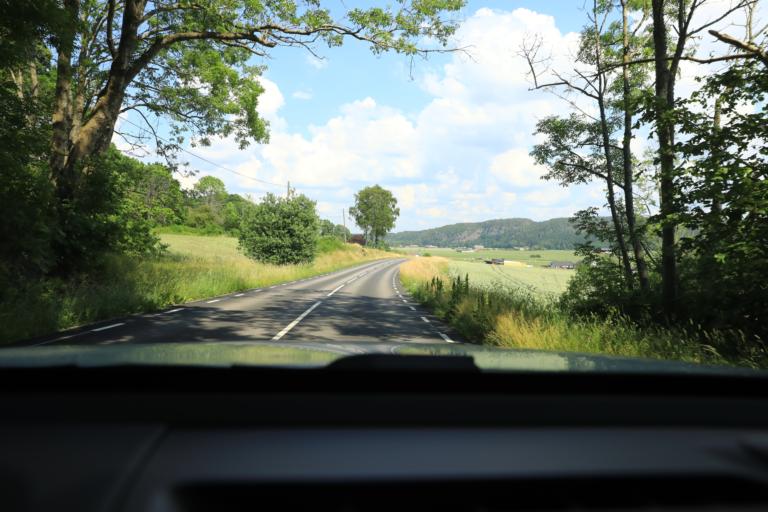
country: SE
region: Halland
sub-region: Varbergs Kommun
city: Veddige
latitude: 57.2079
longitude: 12.3023
